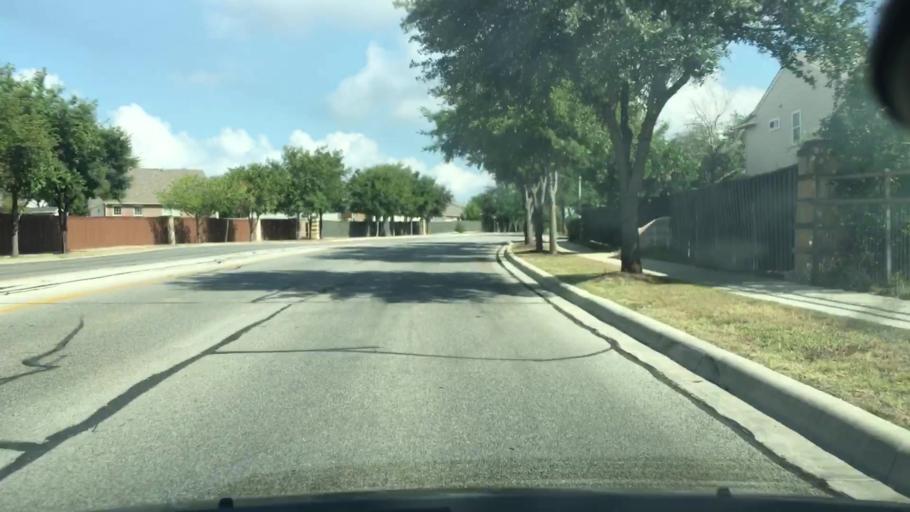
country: US
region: Texas
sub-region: Guadalupe County
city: Cibolo
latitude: 29.5809
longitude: -98.2462
